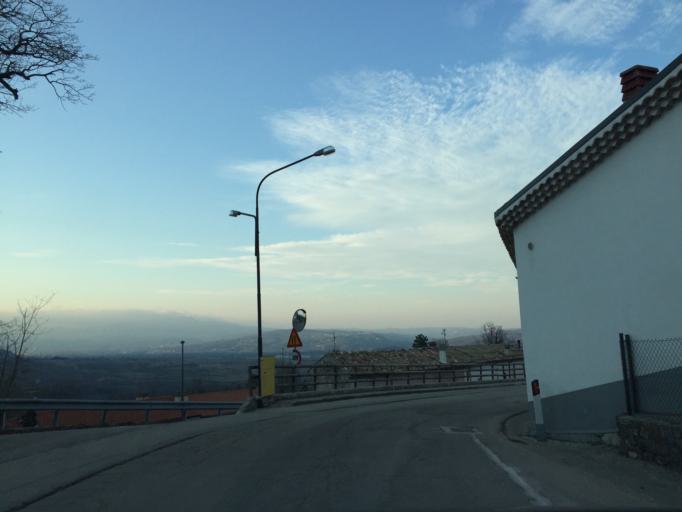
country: IT
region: Molise
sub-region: Provincia di Campobasso
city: Guardiaregia
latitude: 41.4364
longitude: 14.5449
